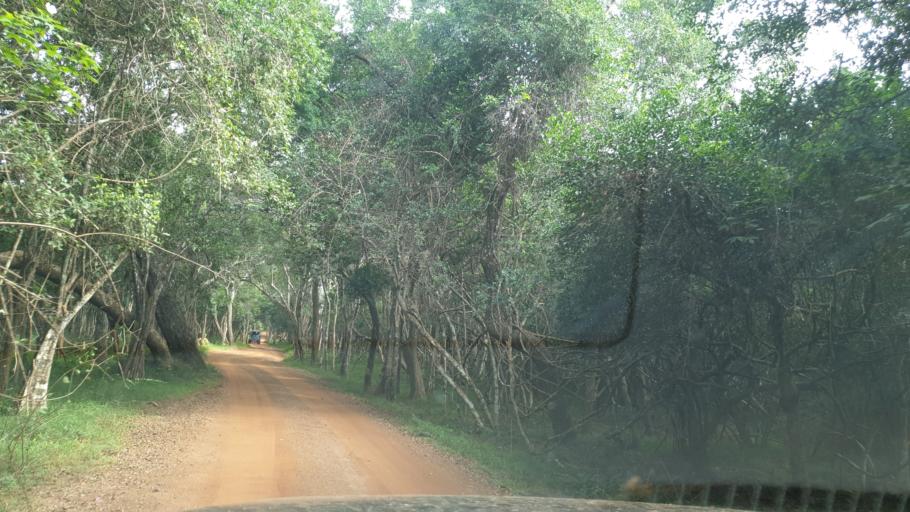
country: LK
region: North Central
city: Anuradhapura
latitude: 8.4104
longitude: 80.0392
